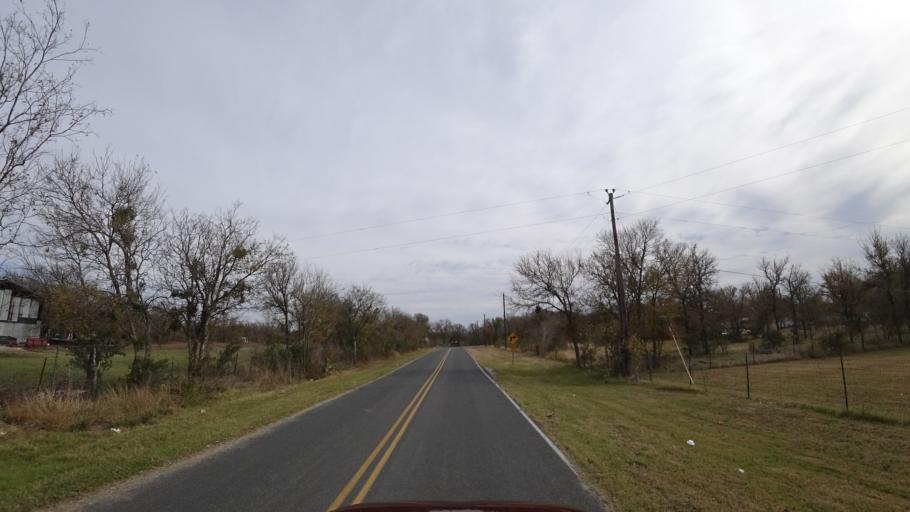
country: US
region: Texas
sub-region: Travis County
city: Garfield
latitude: 30.1379
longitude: -97.5761
